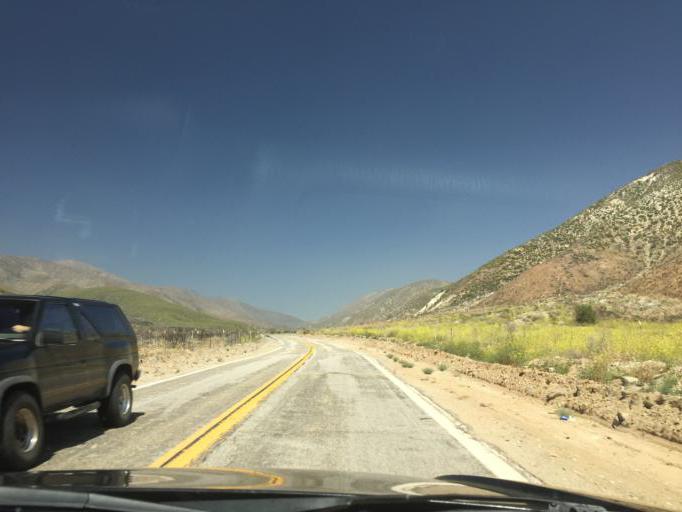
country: US
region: California
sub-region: San Bernardino County
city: Wrightwood
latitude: 34.3057
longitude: -117.5247
